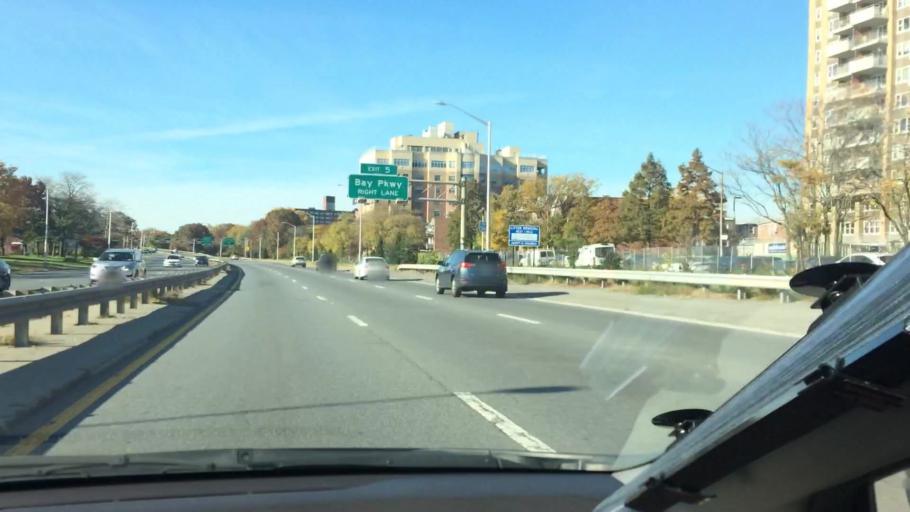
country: US
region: New York
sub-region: Kings County
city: Bensonhurst
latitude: 40.5927
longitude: -73.9952
